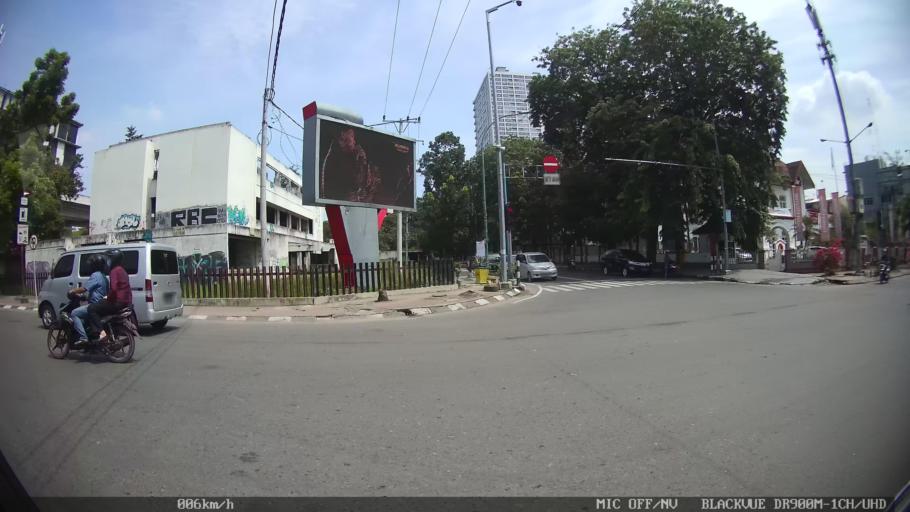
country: ID
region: North Sumatra
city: Medan
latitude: 3.5936
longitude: 98.6793
